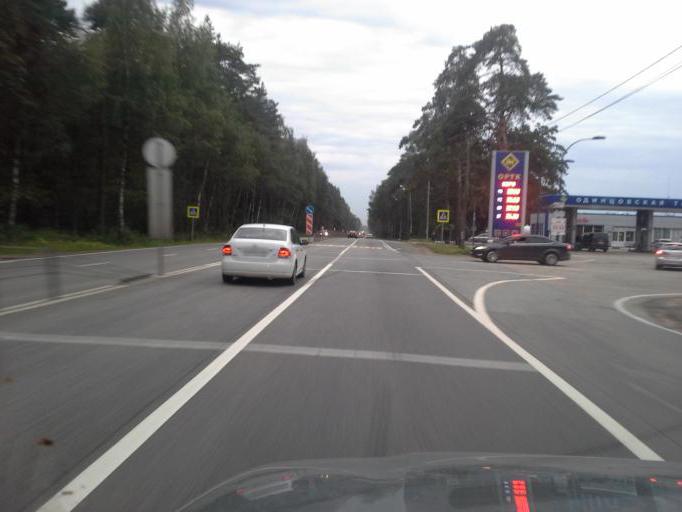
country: RU
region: Moskovskaya
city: Zhavoronki
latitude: 55.6478
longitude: 37.0764
